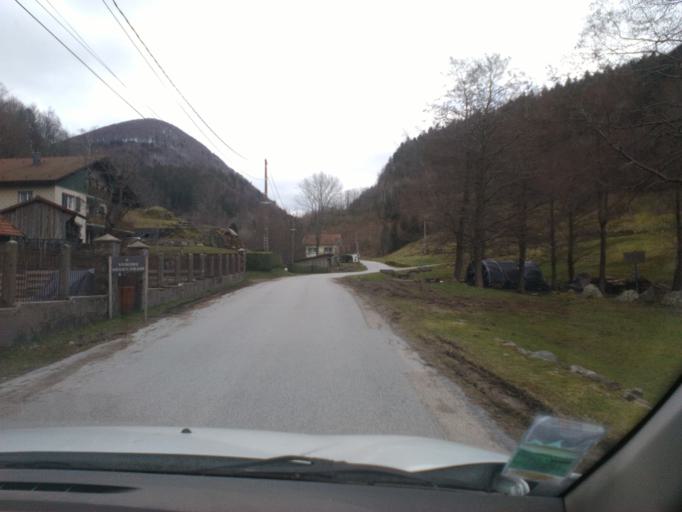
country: FR
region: Lorraine
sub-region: Departement des Vosges
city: Bussang
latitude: 47.8894
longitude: 6.8840
